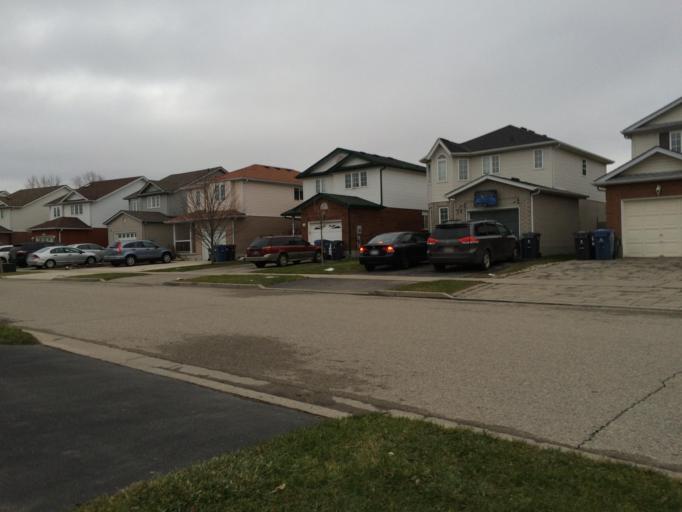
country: CA
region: Ontario
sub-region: Wellington County
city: Guelph
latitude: 43.5261
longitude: -80.2769
